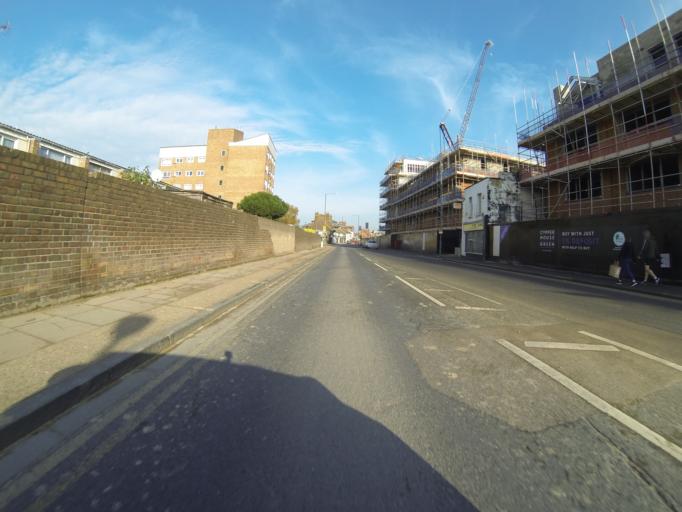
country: GB
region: England
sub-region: Kent
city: Dartford
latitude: 51.4403
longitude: 0.2153
